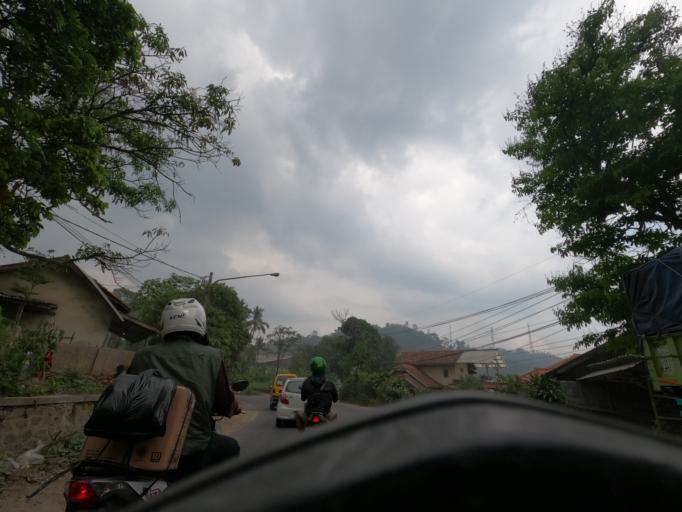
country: ID
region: West Java
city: Padalarang
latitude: -6.8313
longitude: 107.4532
